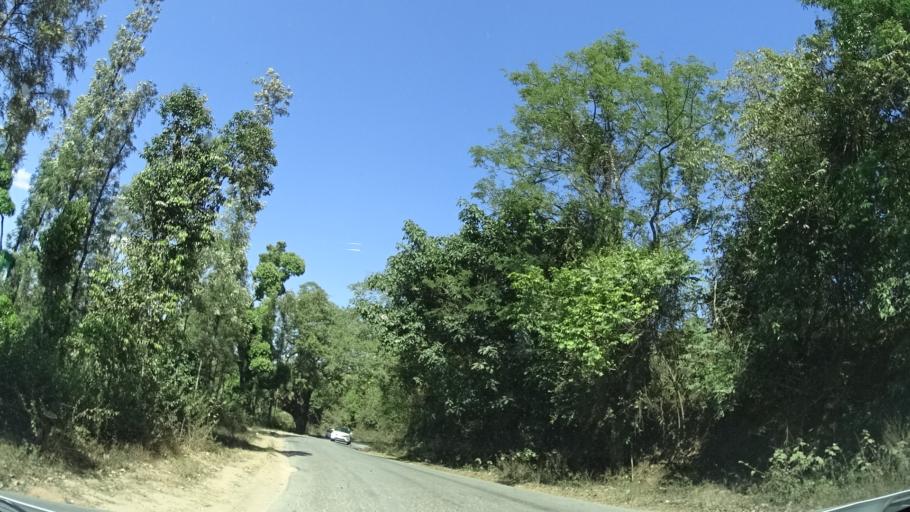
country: IN
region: Karnataka
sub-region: Chikmagalur
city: Mudigere
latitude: 13.1976
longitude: 75.6706
